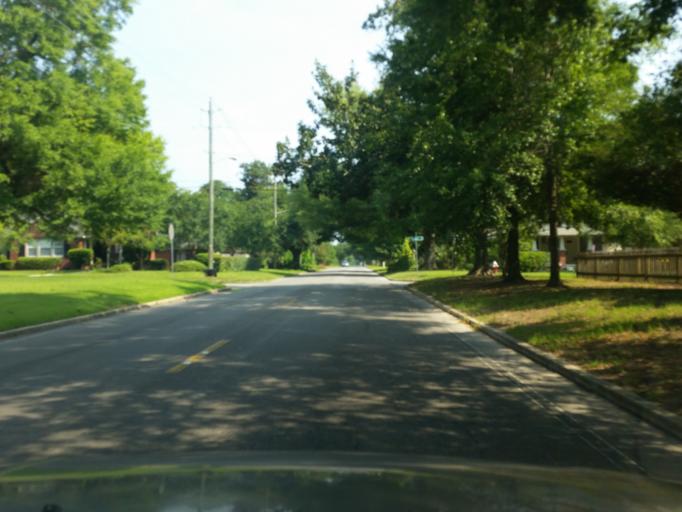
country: US
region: Florida
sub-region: Escambia County
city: East Pensacola Heights
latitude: 30.4379
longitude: -87.1982
